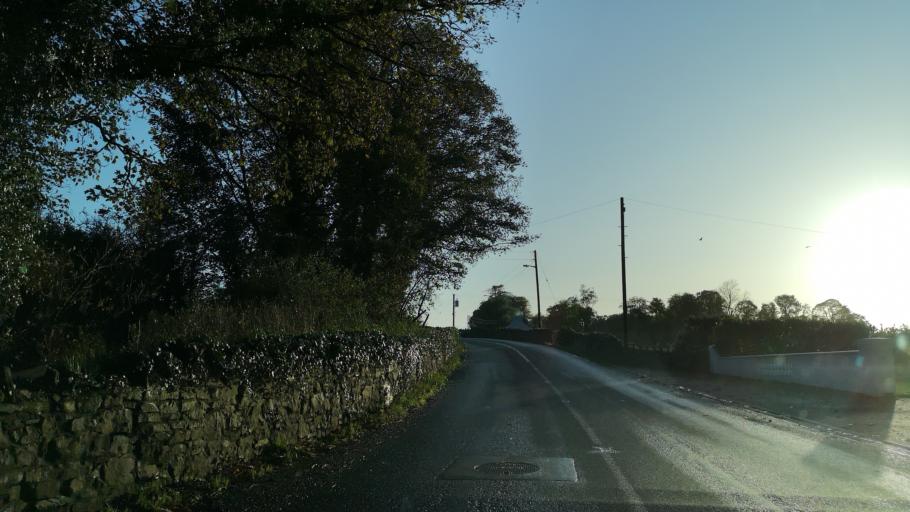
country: IE
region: Connaught
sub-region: Roscommon
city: Castlerea
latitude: 53.7659
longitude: -8.5032
